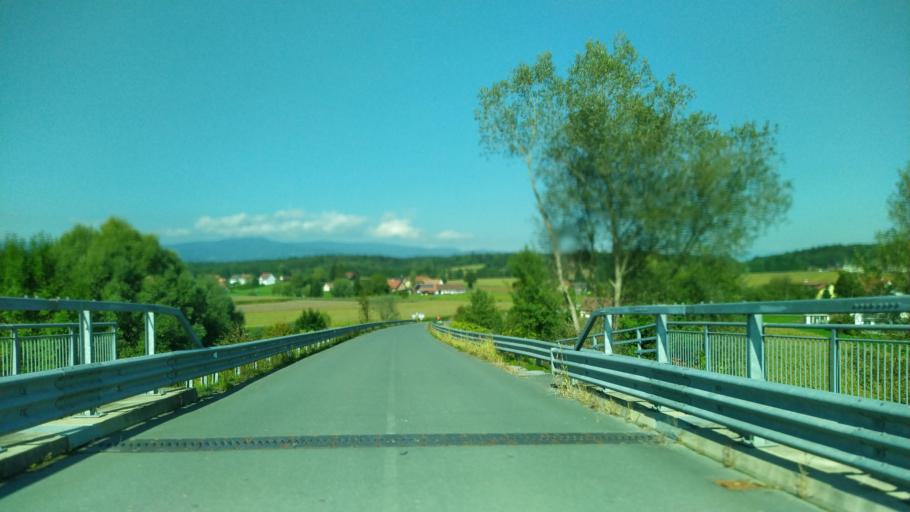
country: AT
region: Styria
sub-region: Politischer Bezirk Deutschlandsberg
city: Gross Sankt Florian
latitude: 46.8277
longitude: 15.3493
